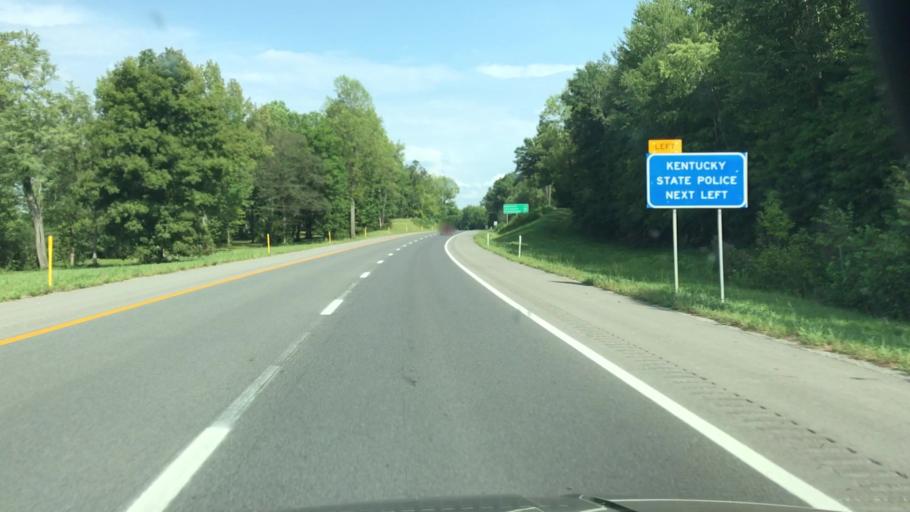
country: US
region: Kentucky
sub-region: Hopkins County
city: Nortonville
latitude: 37.2120
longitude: -87.4268
